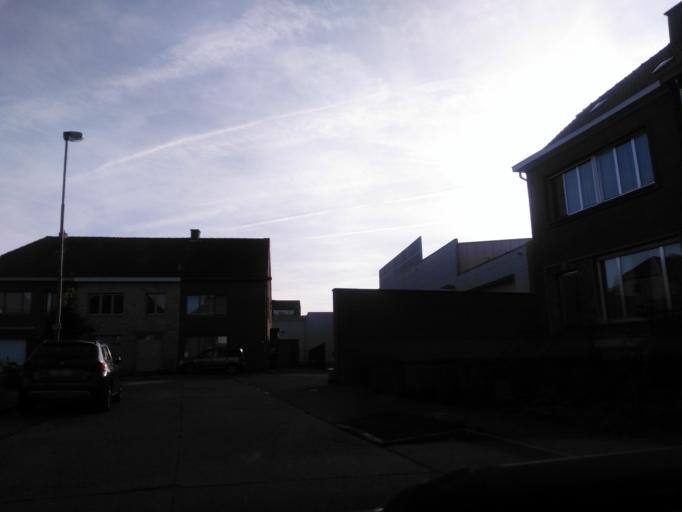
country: BE
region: Flanders
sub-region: Provincie Oost-Vlaanderen
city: Beveren
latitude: 51.2152
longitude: 4.2550
